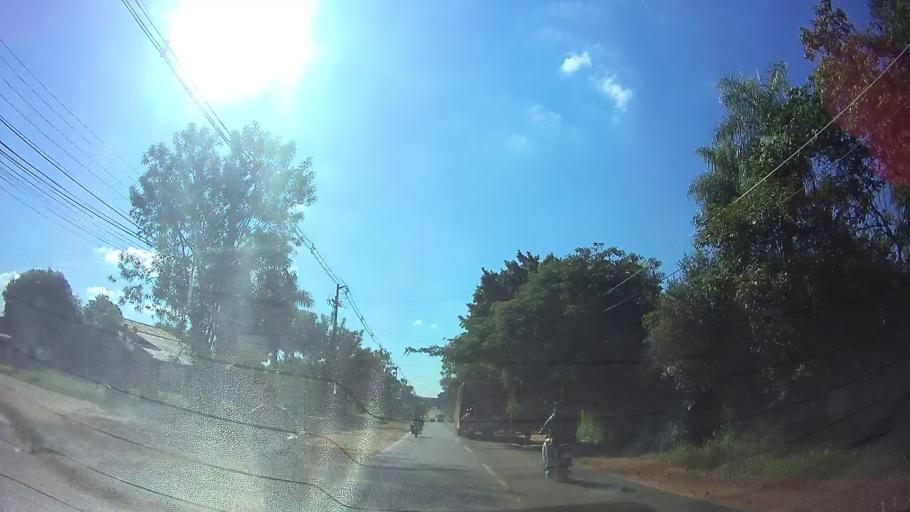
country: PY
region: Central
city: Limpio
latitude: -25.2333
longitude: -57.4754
